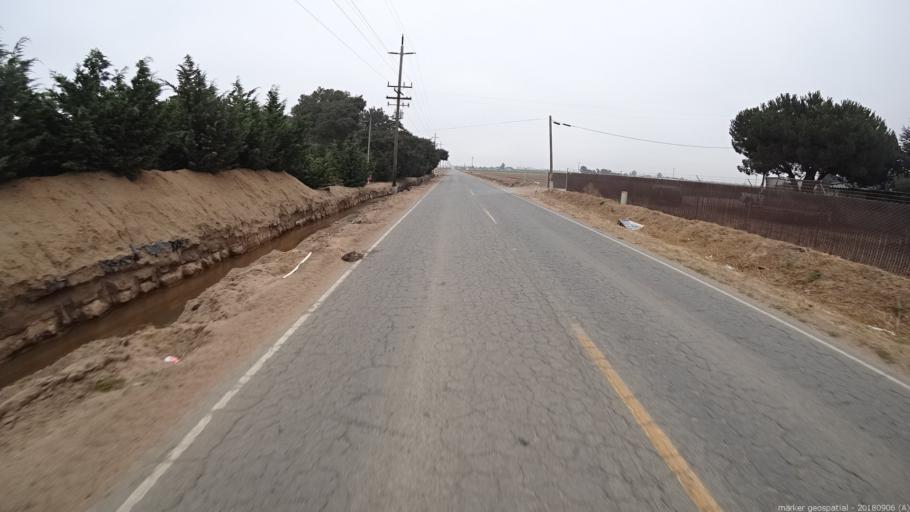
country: US
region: California
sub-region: Monterey County
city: Chualar
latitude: 36.6377
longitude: -121.5625
